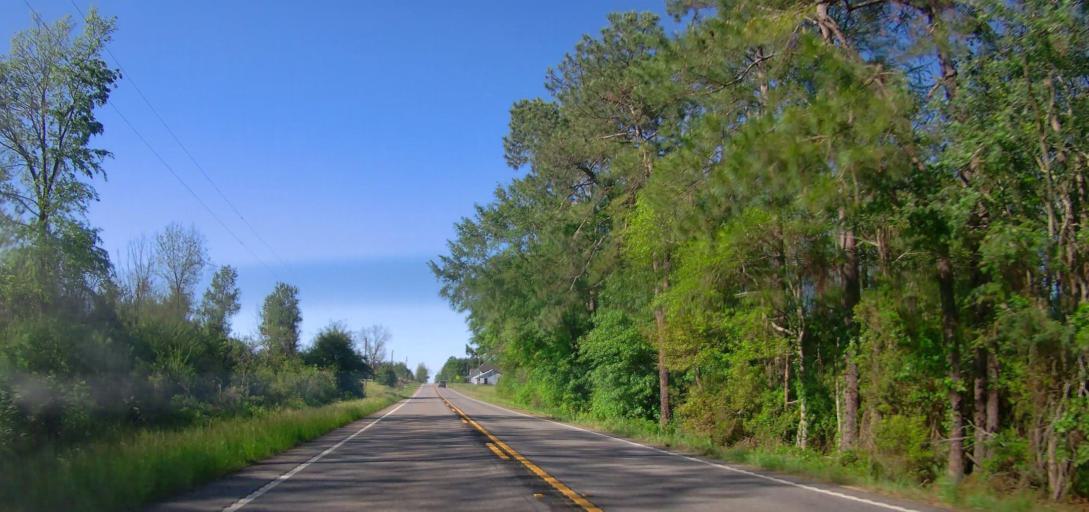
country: US
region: Georgia
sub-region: Wilcox County
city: Rochelle
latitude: 31.8193
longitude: -83.4891
